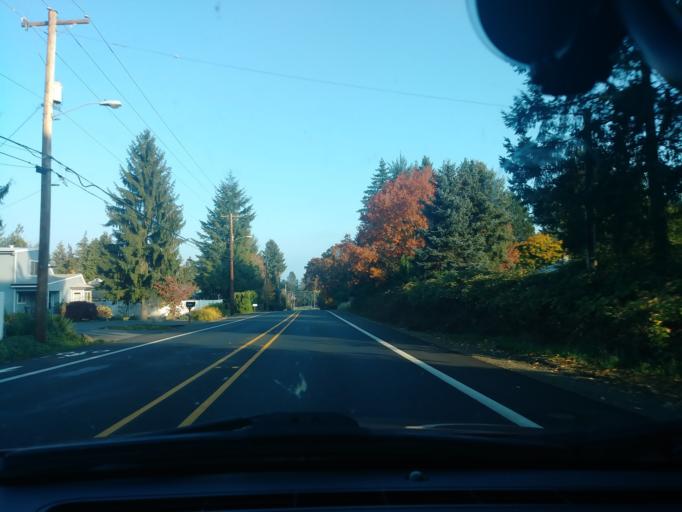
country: US
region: Oregon
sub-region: Washington County
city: Forest Grove
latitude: 45.5303
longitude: -123.1304
